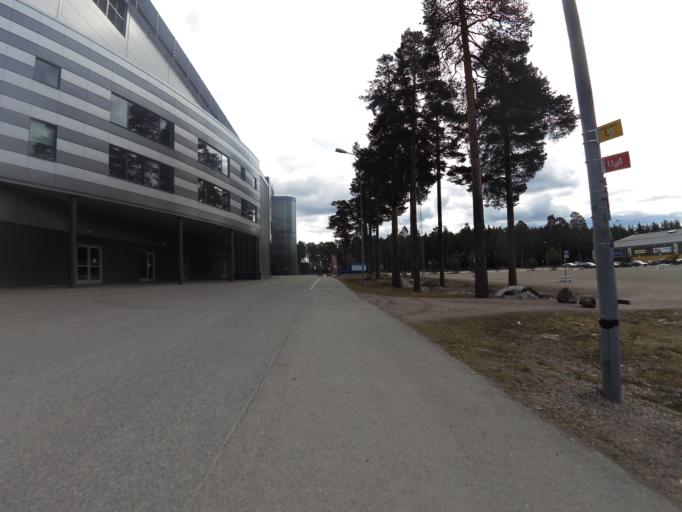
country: SE
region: Gaevleborg
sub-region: Gavle Kommun
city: Gavle
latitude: 60.6912
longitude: 17.1312
